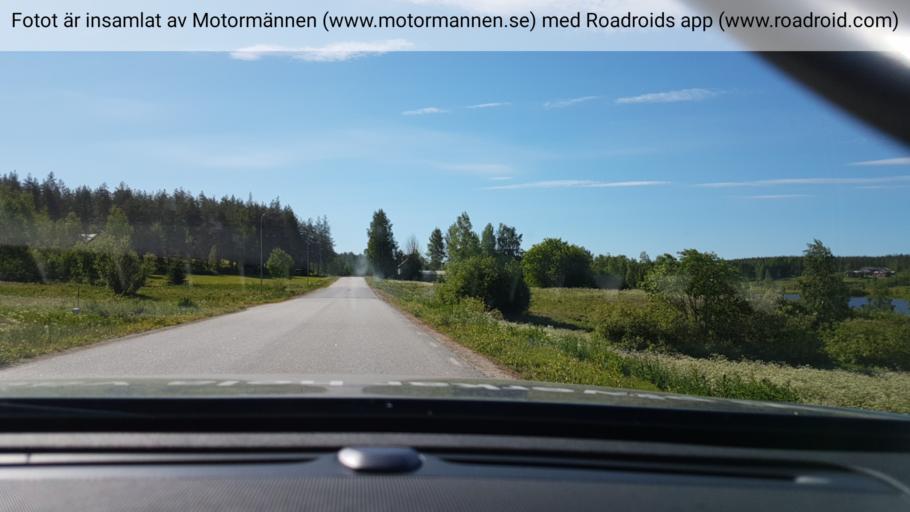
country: SE
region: Vaesterbotten
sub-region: Bjurholms Kommun
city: Bjurholm
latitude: 64.0213
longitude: 19.3495
